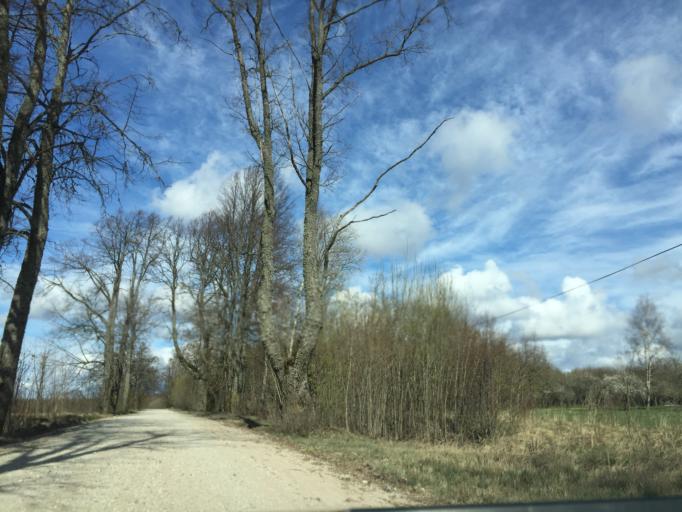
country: LV
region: Limbazu Rajons
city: Limbazi
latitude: 57.5719
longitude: 24.5933
